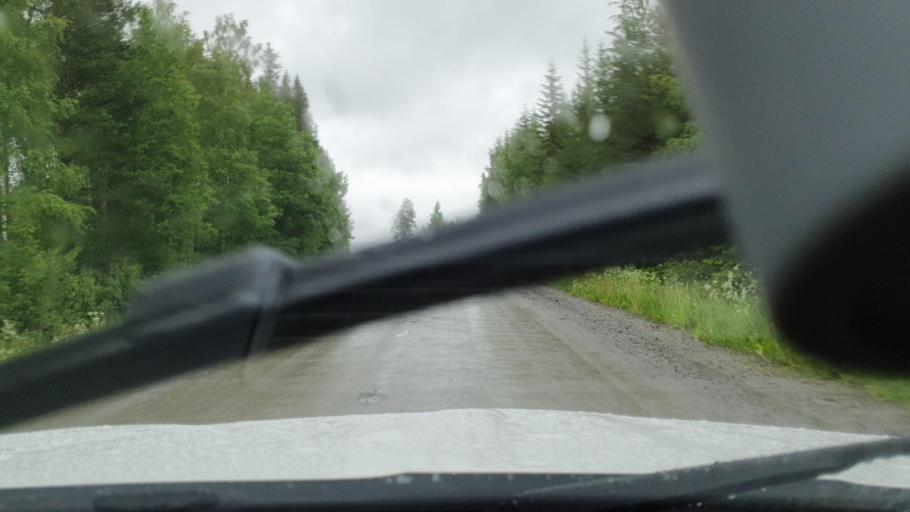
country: SE
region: Vaesterbotten
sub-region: Skelleftea Kommun
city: Burtraesk
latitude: 64.3582
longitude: 20.4438
